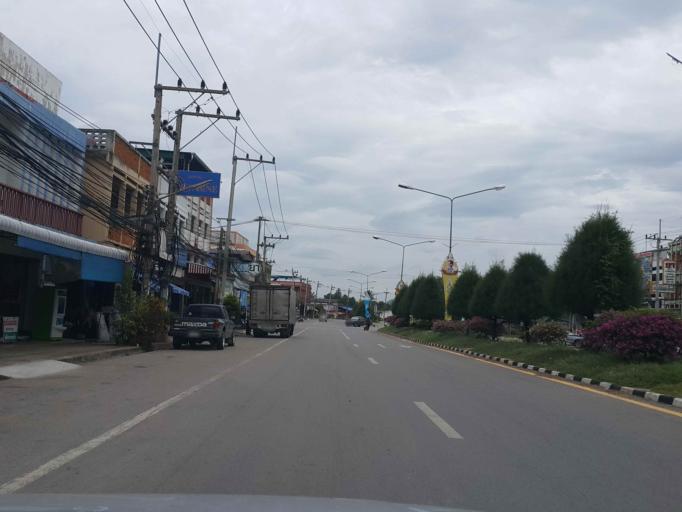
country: TH
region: Lampang
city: Thoen
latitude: 17.6396
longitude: 99.2356
